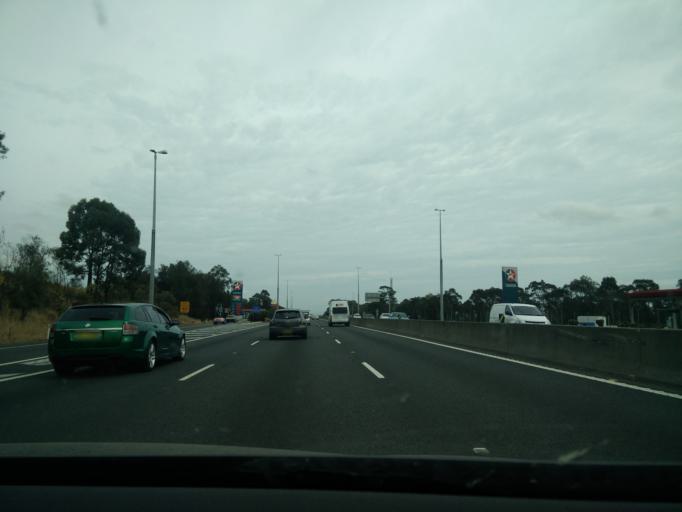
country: AU
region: New South Wales
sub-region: Blacktown
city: Doonside
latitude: -33.8022
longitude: 150.8866
